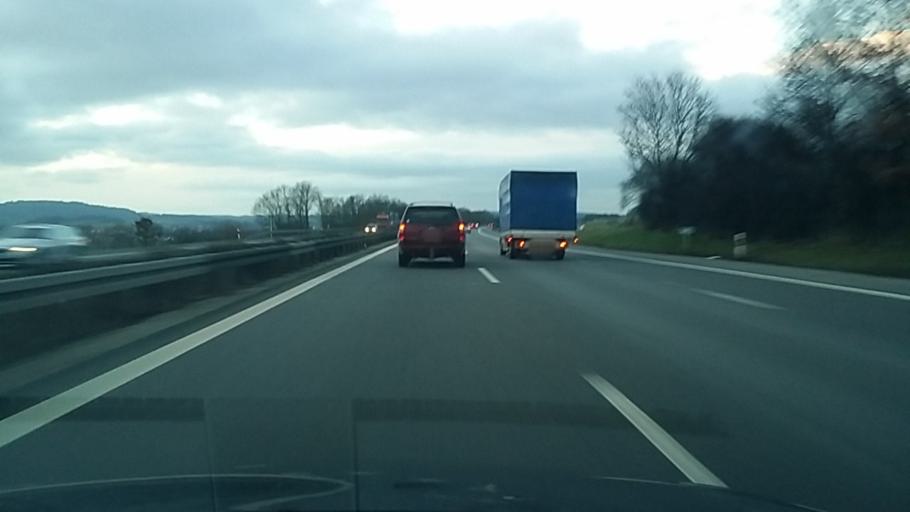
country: DE
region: Bavaria
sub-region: Upper Palatinate
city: Pilsach
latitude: 49.3190
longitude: 11.4690
